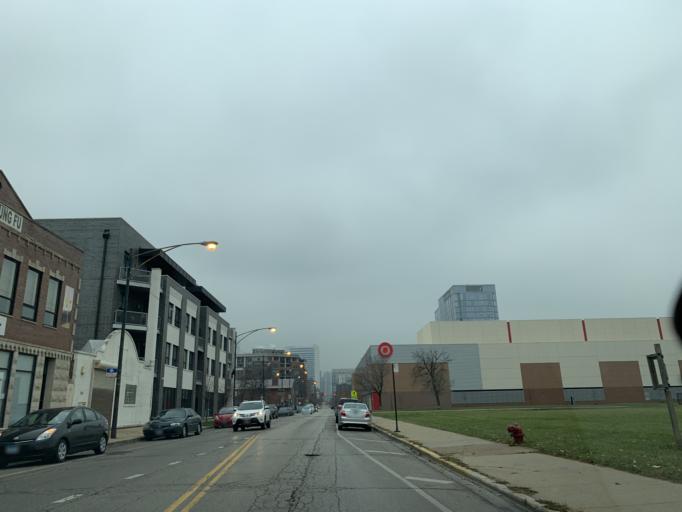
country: US
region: Illinois
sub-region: Cook County
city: Chicago
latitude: 41.9060
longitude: -87.6433
